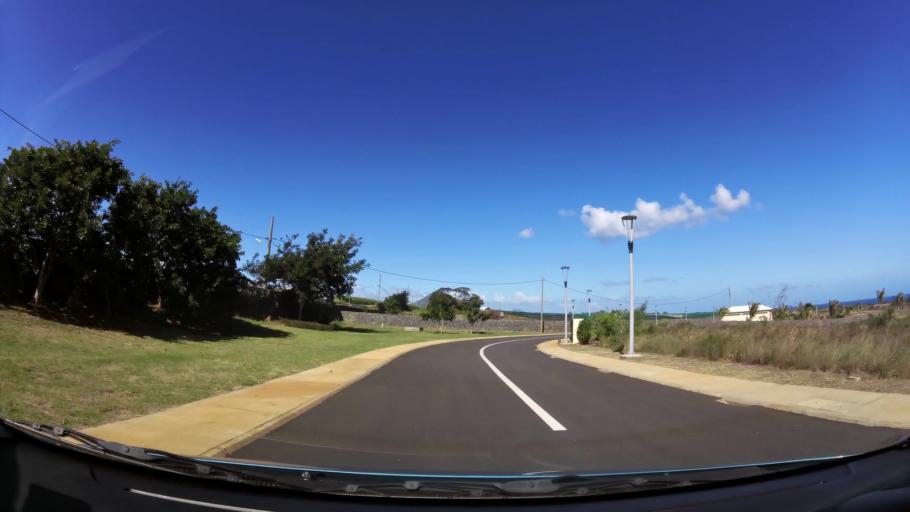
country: MU
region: Black River
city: Flic en Flac
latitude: -20.2701
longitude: 57.3871
